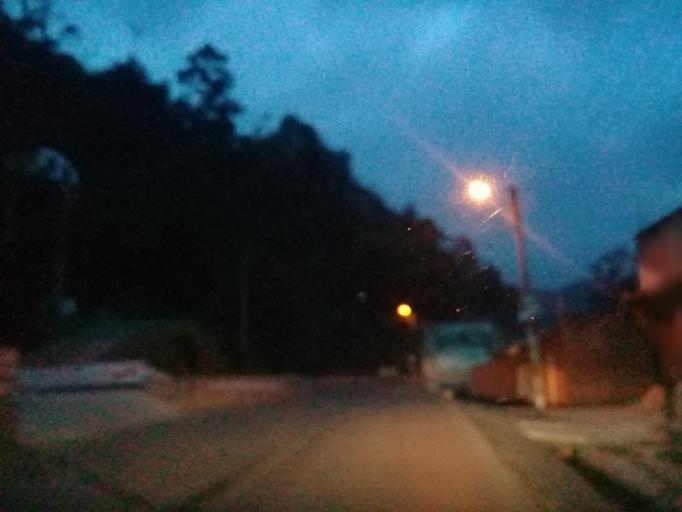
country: CO
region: Cundinamarca
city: Pacho
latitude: 5.1339
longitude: -74.1537
